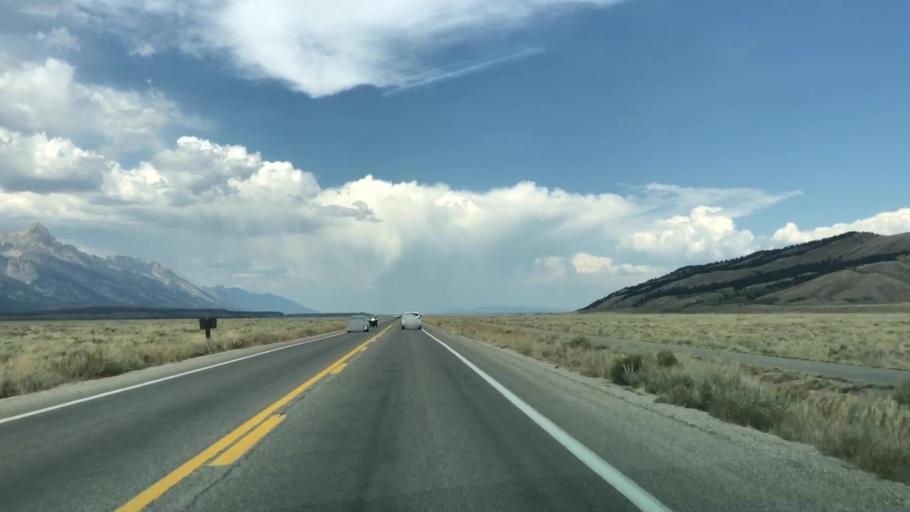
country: US
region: Wyoming
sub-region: Teton County
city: Jackson
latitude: 43.6032
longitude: -110.7239
